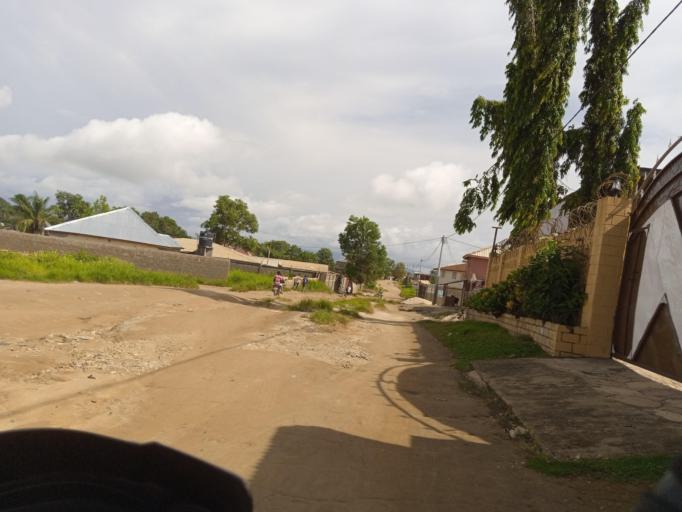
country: SL
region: Northern Province
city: Masoyila
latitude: 8.6115
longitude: -13.2021
